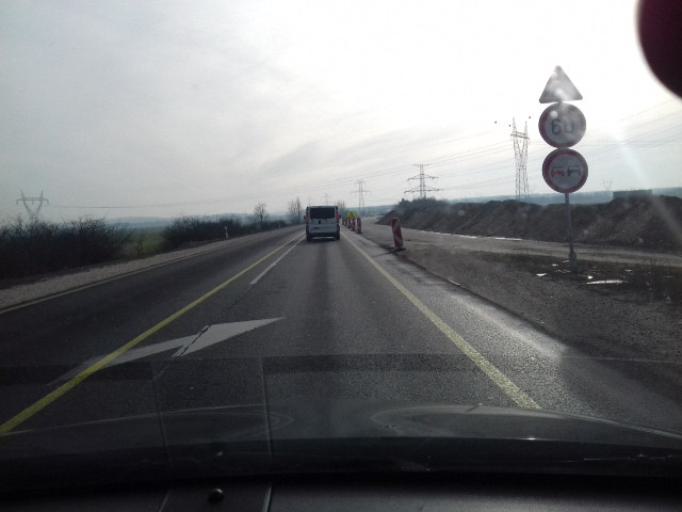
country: HU
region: Pest
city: Szod
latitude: 47.6919
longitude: 19.1731
